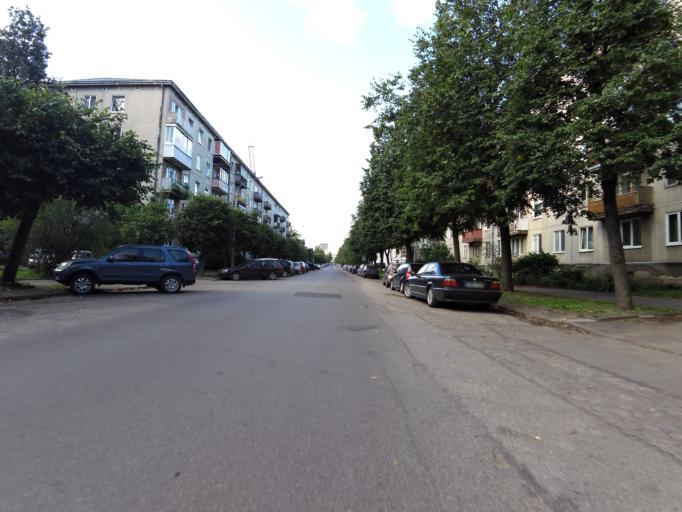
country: LT
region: Vilnius County
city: Naujamiestis
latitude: 54.6729
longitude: 25.2625
